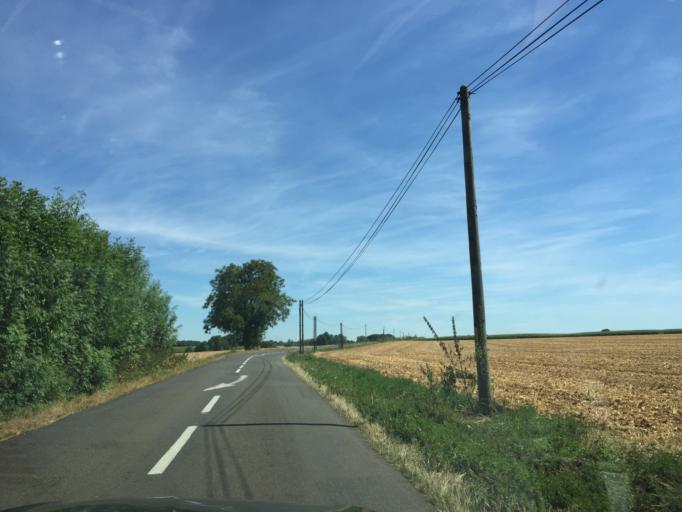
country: FR
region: Poitou-Charentes
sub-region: Departement de la Vienne
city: Iteuil
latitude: 46.4378
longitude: 0.3145
